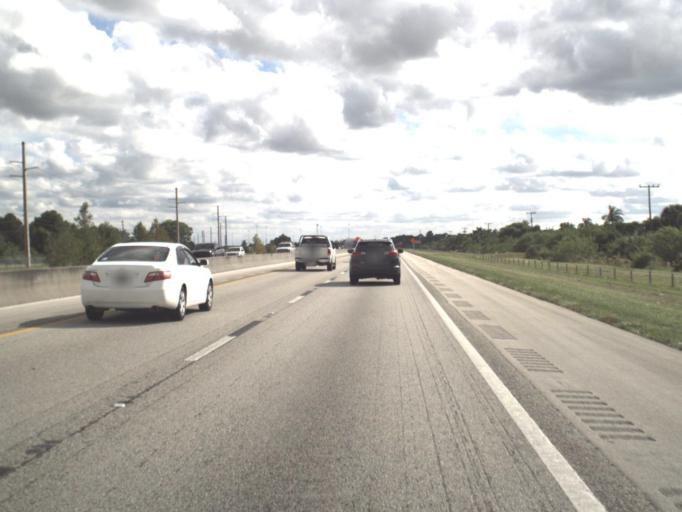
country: US
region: Florida
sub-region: Saint Lucie County
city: River Park
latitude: 27.3153
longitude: -80.3744
